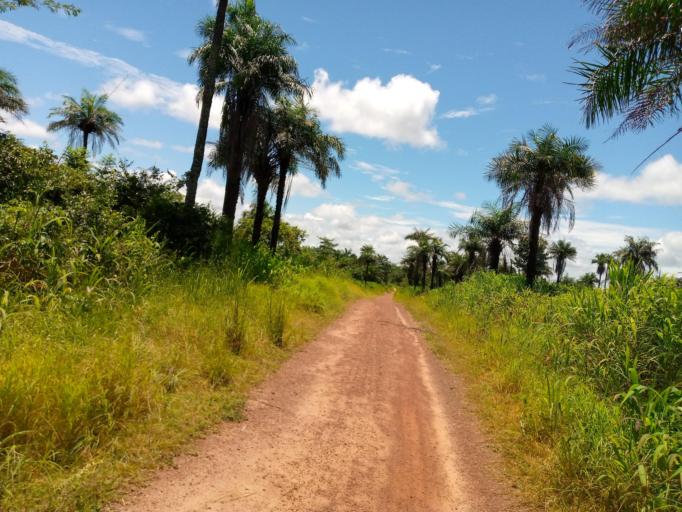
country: SL
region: Northern Province
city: Makeni
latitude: 9.0520
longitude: -12.1546
